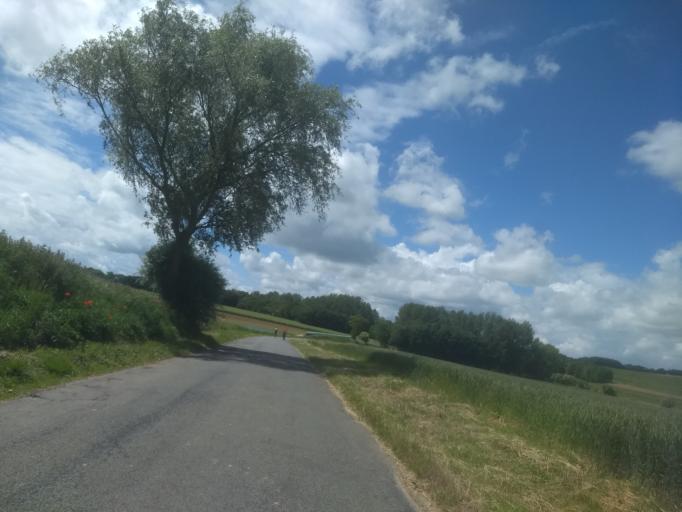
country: FR
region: Nord-Pas-de-Calais
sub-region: Departement du Pas-de-Calais
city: Beaumetz-les-Loges
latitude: 50.2263
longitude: 2.6653
